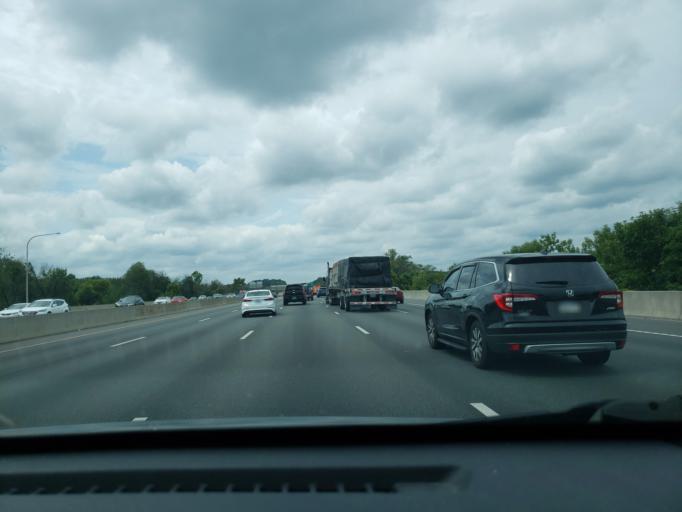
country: US
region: Delaware
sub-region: New Castle County
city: Newport
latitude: 39.6957
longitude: -75.6217
